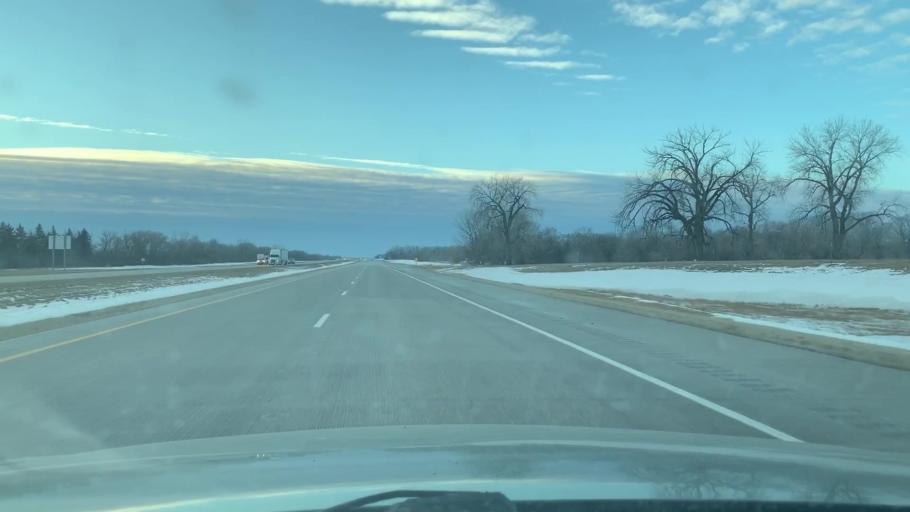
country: US
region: North Dakota
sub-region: Cass County
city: Casselton
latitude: 46.8762
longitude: -97.4324
